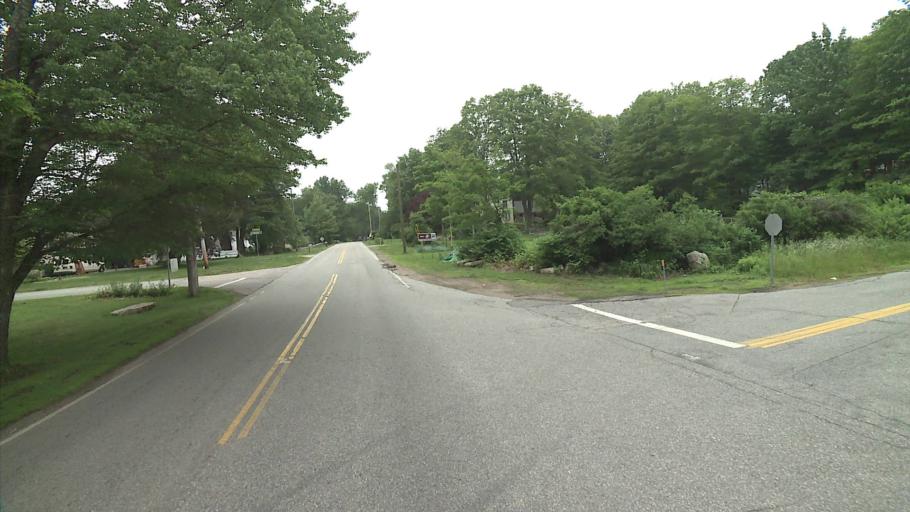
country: US
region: Connecticut
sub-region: Tolland County
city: Hebron
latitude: 41.6863
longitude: -72.3609
